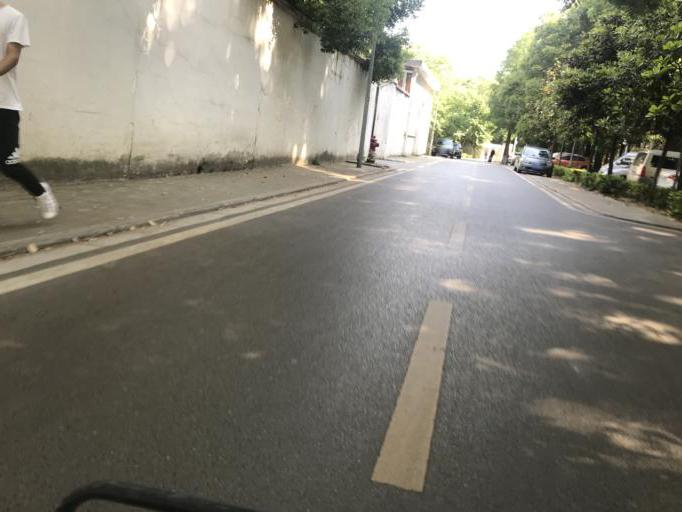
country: CN
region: Hubei
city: Guanshan
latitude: 30.5299
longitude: 114.3574
